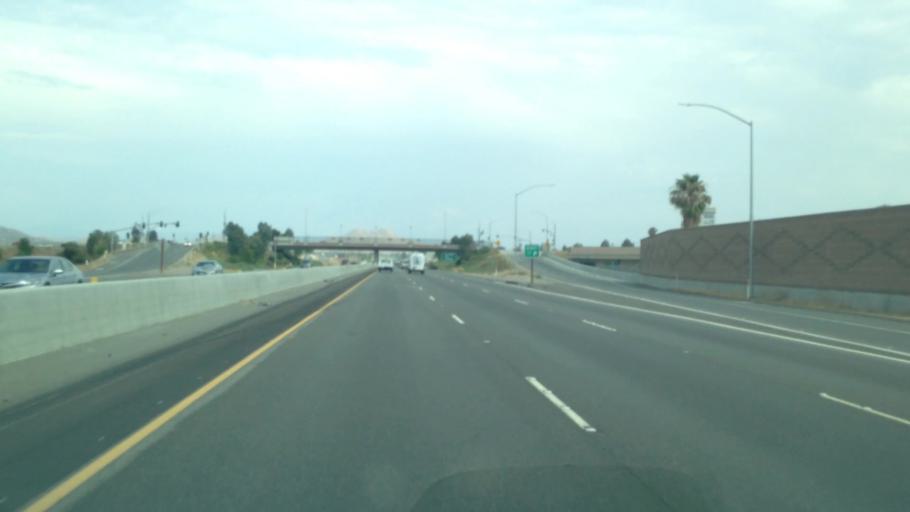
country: US
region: California
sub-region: Riverside County
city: Perris
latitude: 33.7860
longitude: -117.2194
